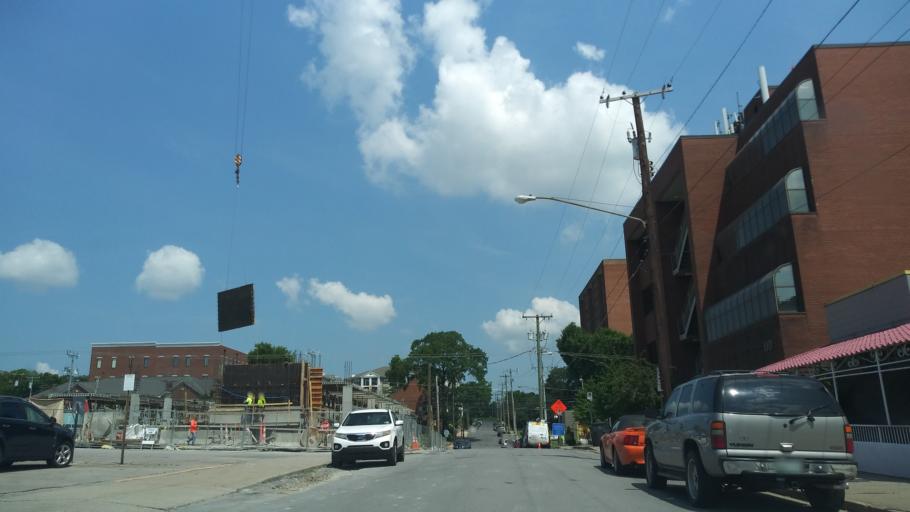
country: US
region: Tennessee
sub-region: Davidson County
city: Nashville
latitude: 36.1451
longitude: -86.8136
